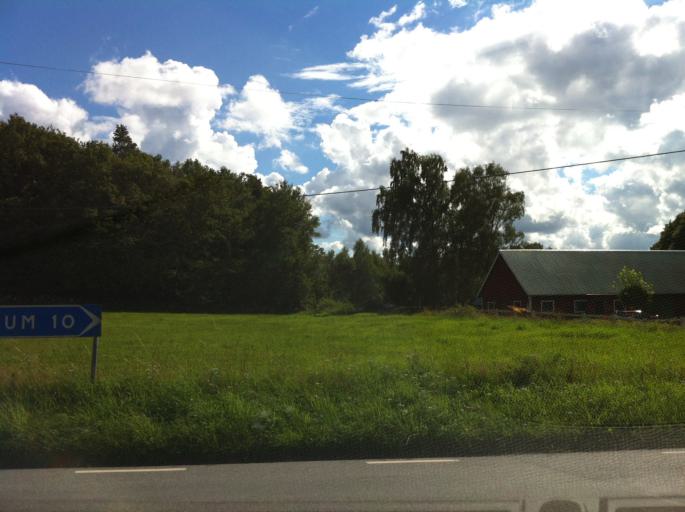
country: SE
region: Skane
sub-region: Hassleholms Kommun
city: Sosdala
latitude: 56.0593
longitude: 13.6548
